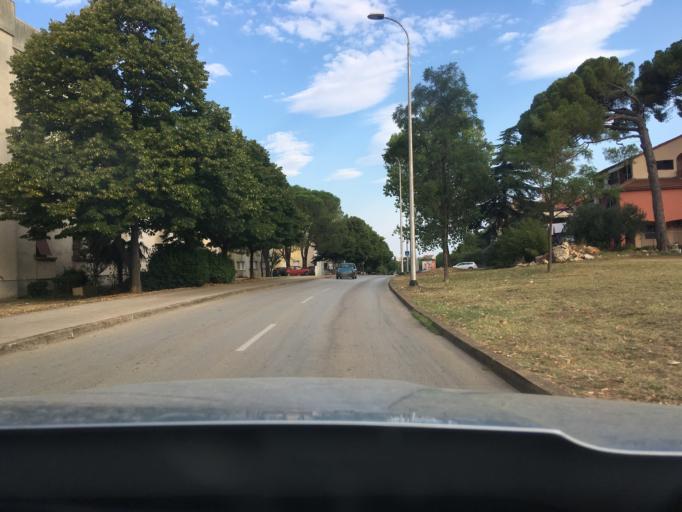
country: HR
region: Zadarska
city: Zadar
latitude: 44.1241
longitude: 15.2313
